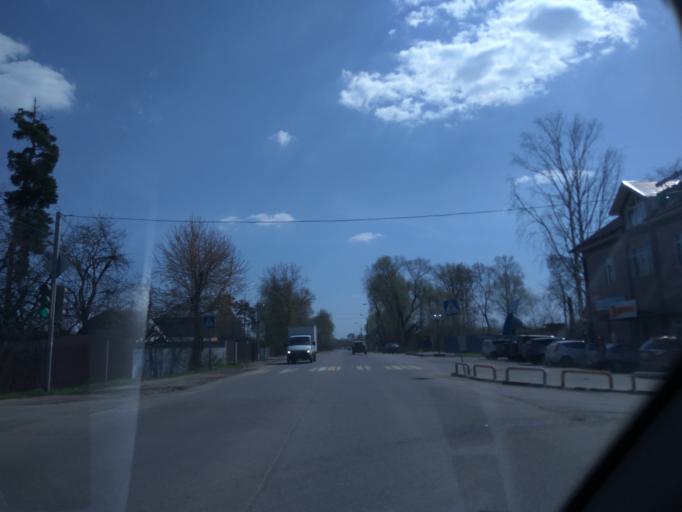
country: RU
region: Moskovskaya
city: Ramenskoye
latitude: 55.5599
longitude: 38.2145
